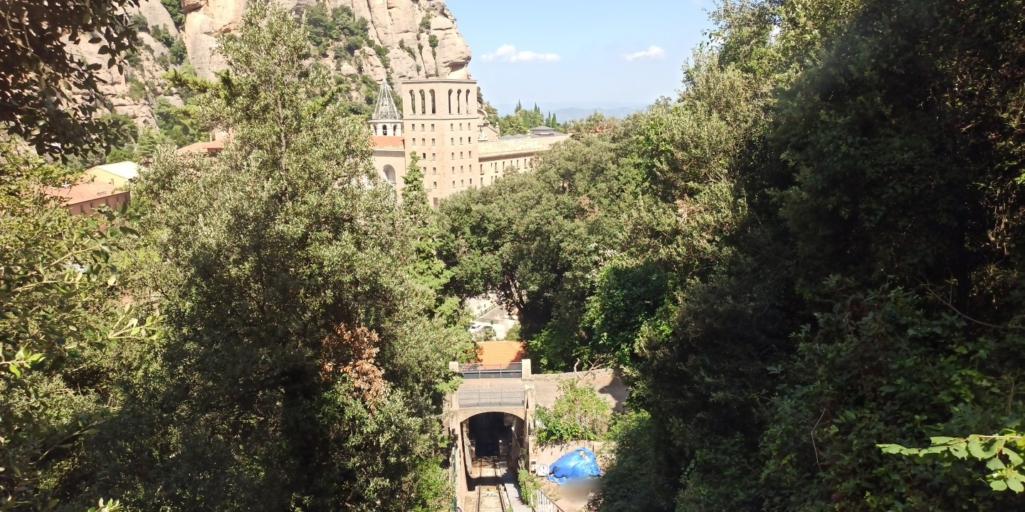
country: ES
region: Catalonia
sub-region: Provincia de Barcelona
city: Collbato
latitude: 41.5915
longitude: 1.8359
